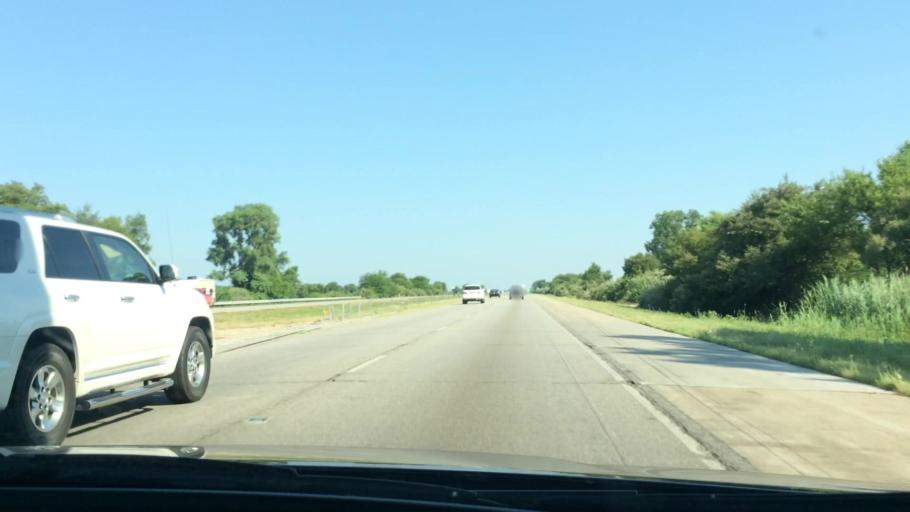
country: US
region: Indiana
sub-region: Jasper County
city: Rensselaer
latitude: 40.9844
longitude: -87.2564
